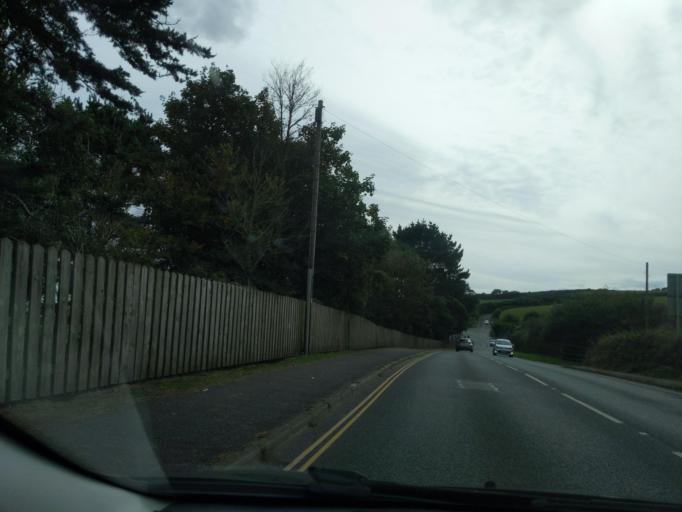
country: GB
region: England
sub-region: Cornwall
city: Mevagissey
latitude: 50.2909
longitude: -4.7862
